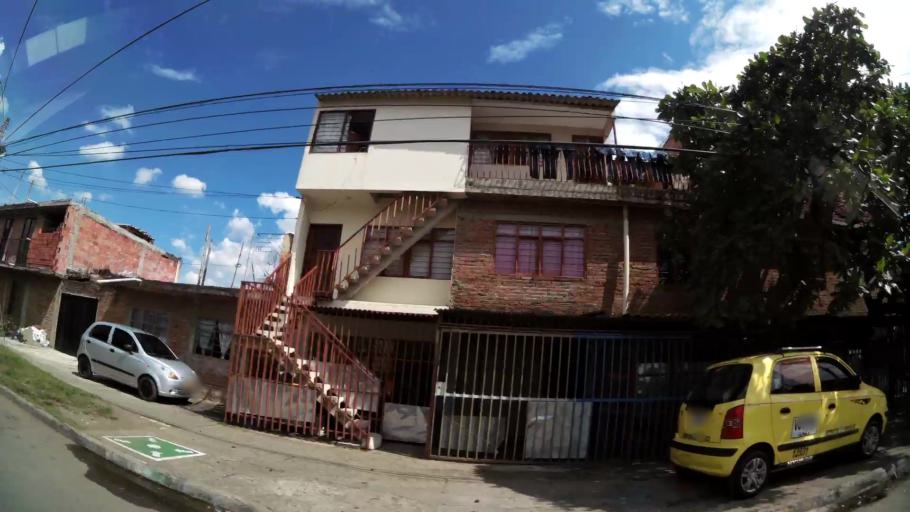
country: CO
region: Valle del Cauca
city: Cali
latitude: 3.4006
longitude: -76.5146
